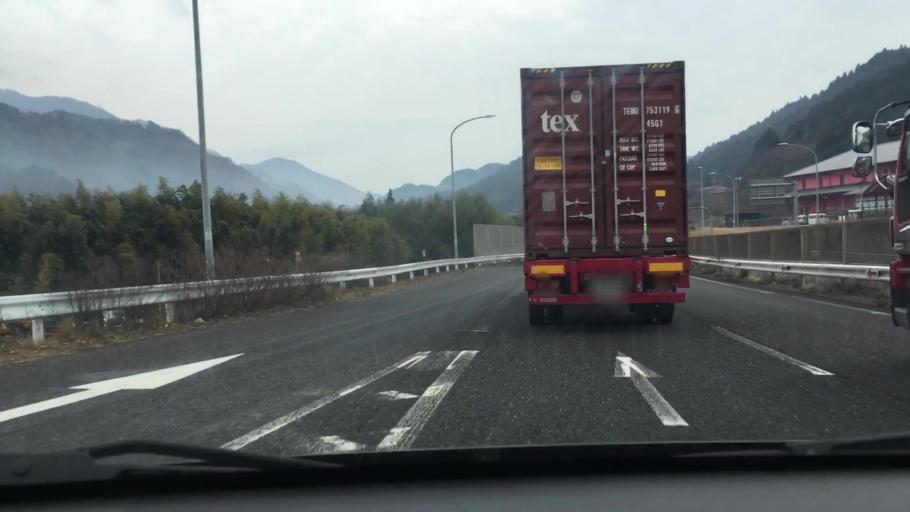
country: JP
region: Mie
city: Ueno-ebisumachi
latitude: 34.8394
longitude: 136.2583
